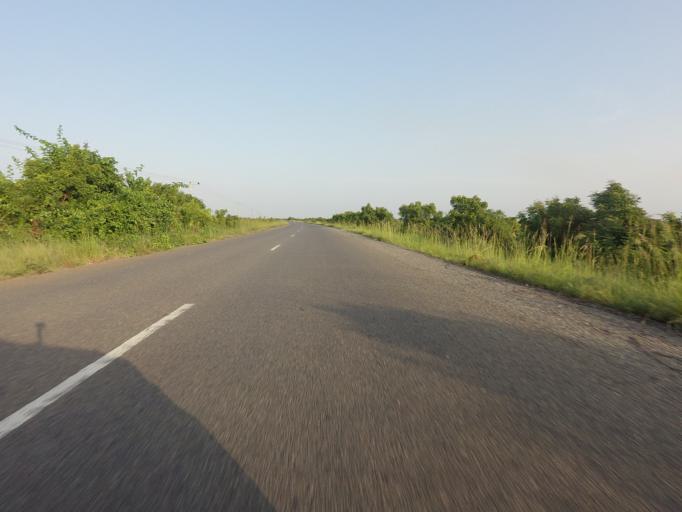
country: GH
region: Volta
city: Anloga
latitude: 5.9649
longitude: 0.6630
